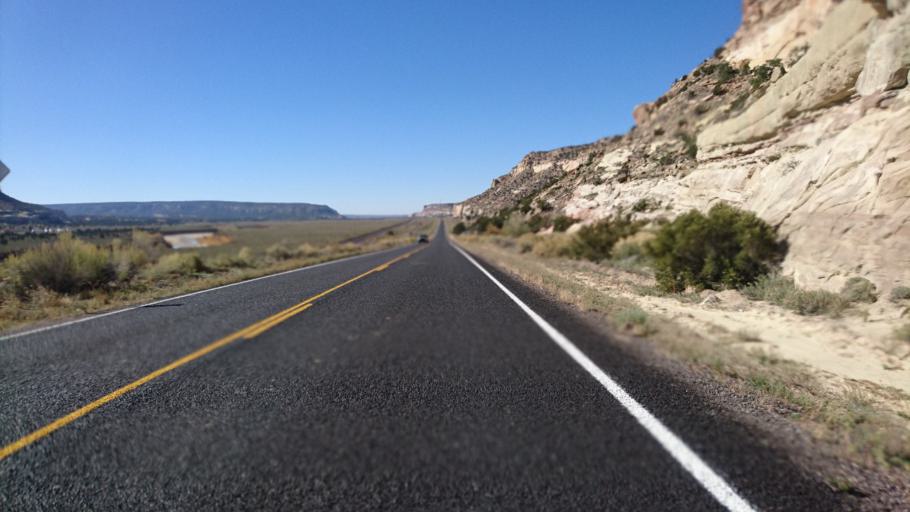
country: US
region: Arizona
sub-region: Apache County
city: Houck
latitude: 35.4113
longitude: -109.0034
